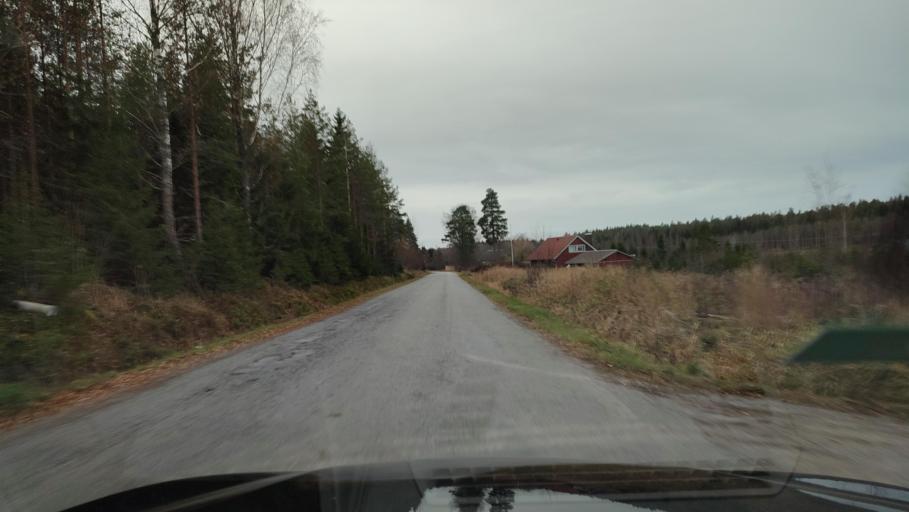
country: FI
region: Ostrobothnia
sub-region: Sydosterbotten
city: Naerpes
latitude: 62.4226
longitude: 21.4090
